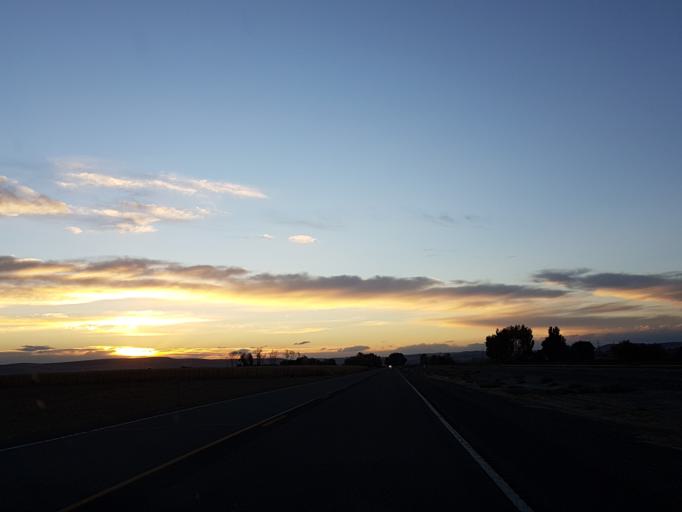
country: US
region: Oregon
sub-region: Malheur County
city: Vale
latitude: 43.9366
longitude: -117.3200
